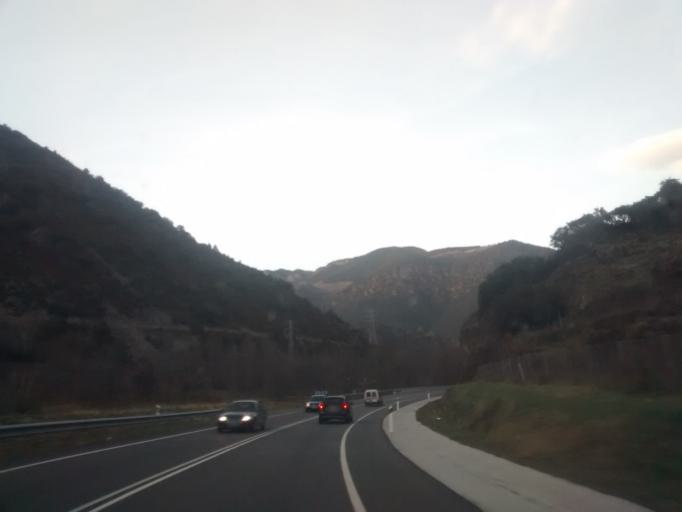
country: ES
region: Catalonia
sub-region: Provincia de Lleida
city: la Seu d'Urgell
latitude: 42.4135
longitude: 1.4648
